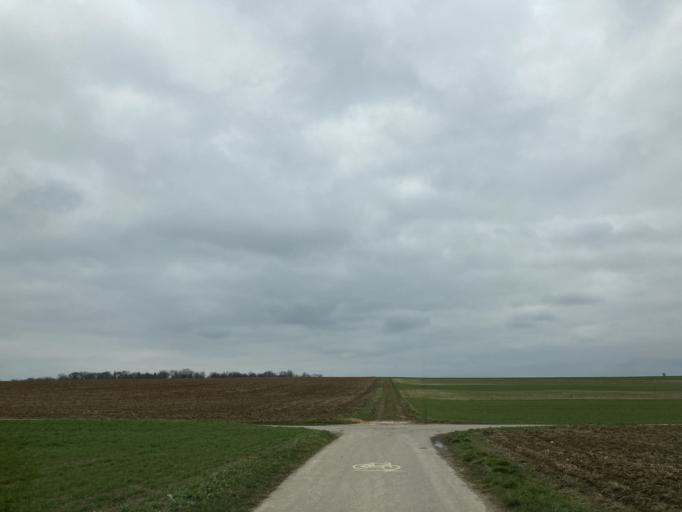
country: DE
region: Baden-Wuerttemberg
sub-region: Tuebingen Region
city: Hirrlingen
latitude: 48.4261
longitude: 8.8982
